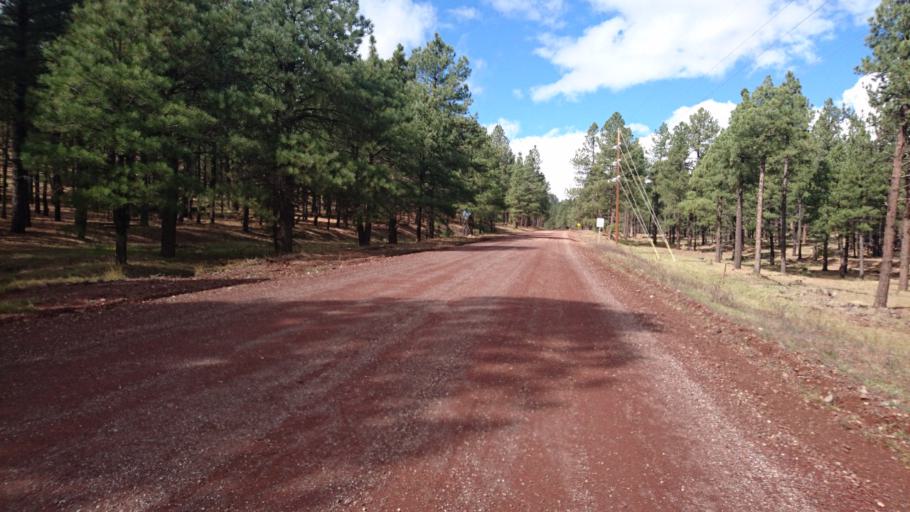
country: US
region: Arizona
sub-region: Coconino County
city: Parks
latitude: 35.2737
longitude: -111.8956
